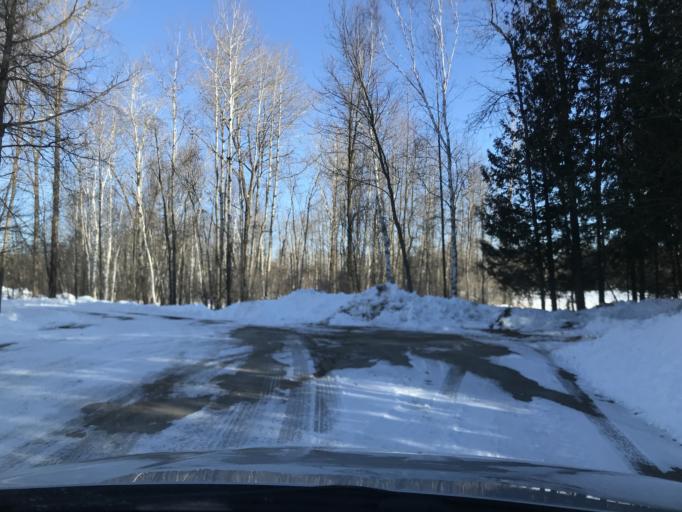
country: US
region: Wisconsin
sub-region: Oconto County
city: Oconto
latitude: 44.9572
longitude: -87.9768
